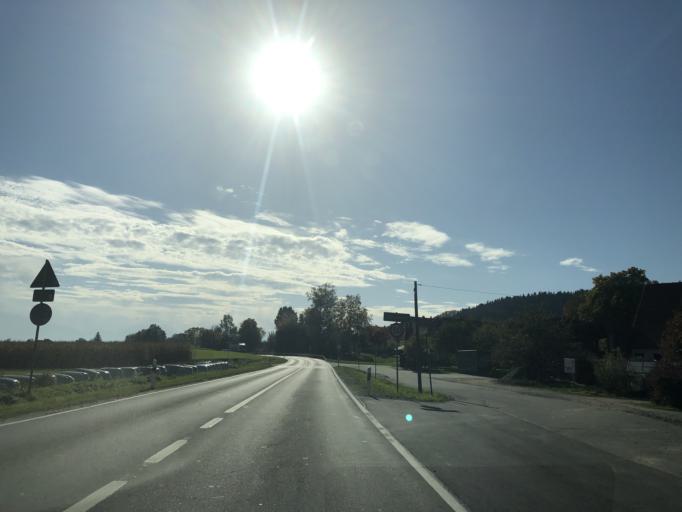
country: DE
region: Bavaria
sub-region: Lower Bavaria
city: Grafling
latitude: 48.8731
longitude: 12.9605
